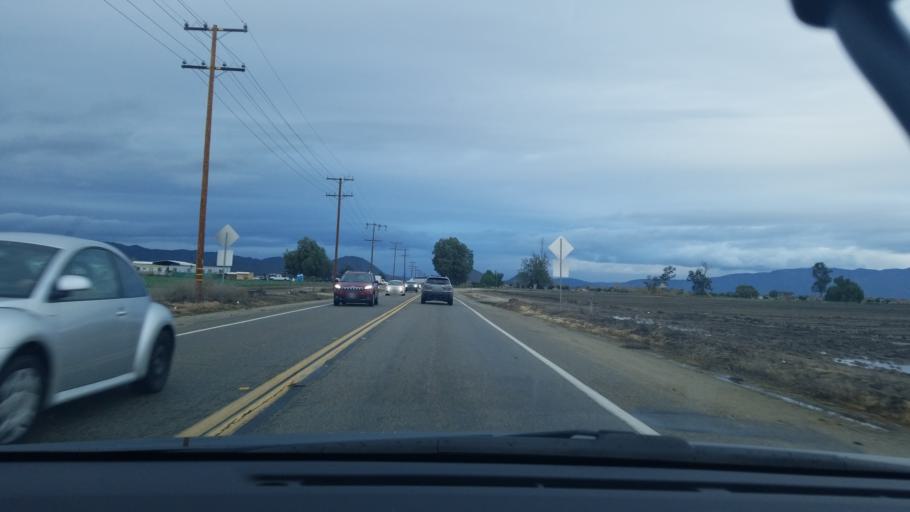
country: US
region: California
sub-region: Riverside County
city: Winchester
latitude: 33.7100
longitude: -117.0326
